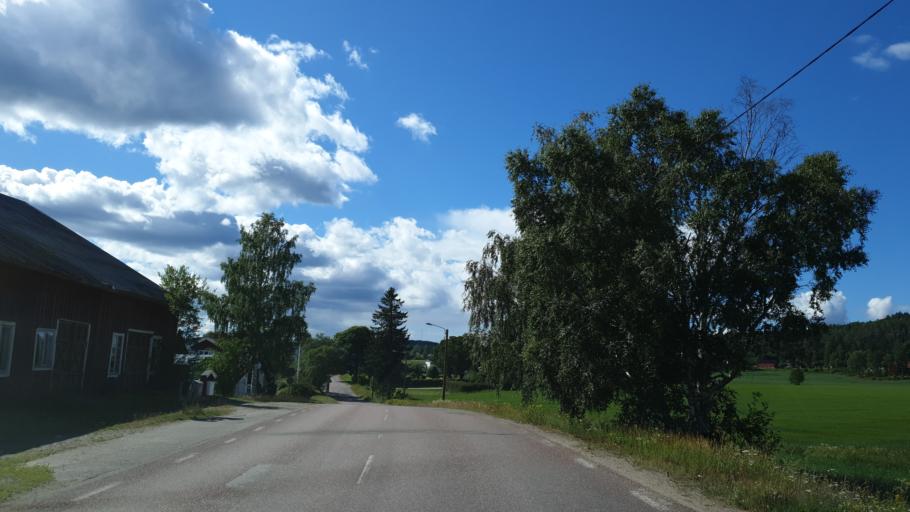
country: SE
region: Gaevleborg
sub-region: Nordanstigs Kommun
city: Bergsjoe
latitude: 62.0510
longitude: 17.2192
